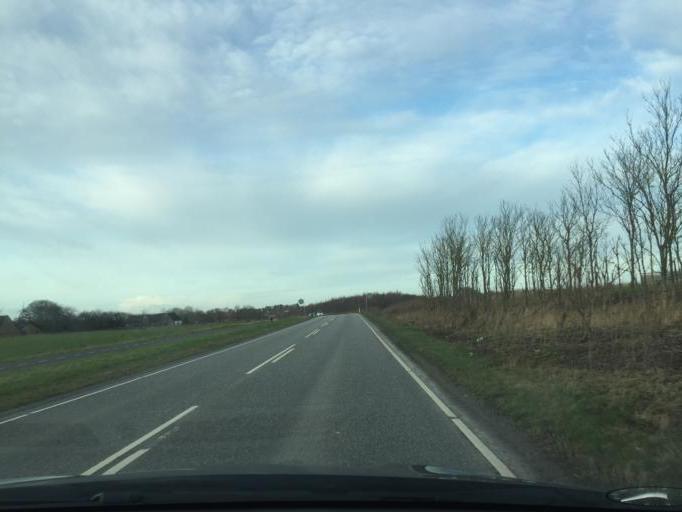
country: DK
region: South Denmark
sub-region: Faaborg-Midtfyn Kommune
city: Ringe
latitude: 55.2509
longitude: 10.4734
